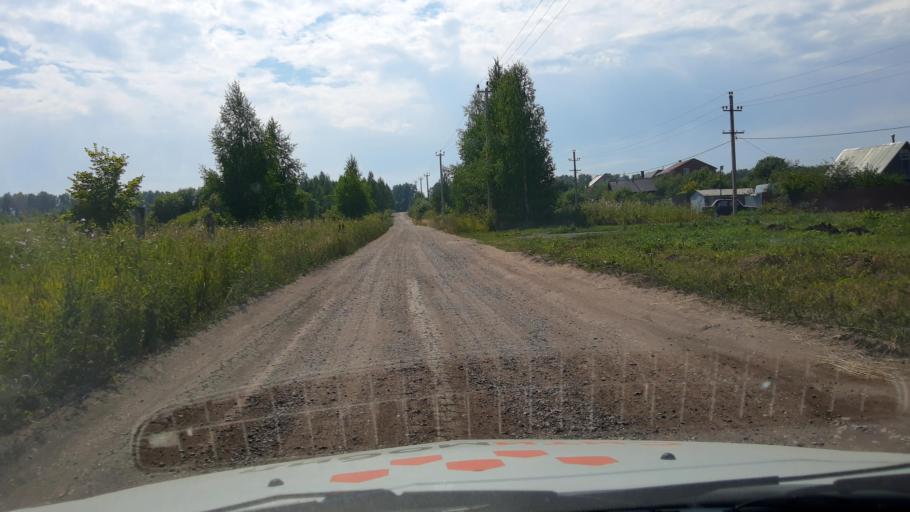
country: RU
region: Bashkortostan
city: Kabakovo
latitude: 54.7074
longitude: 56.1792
